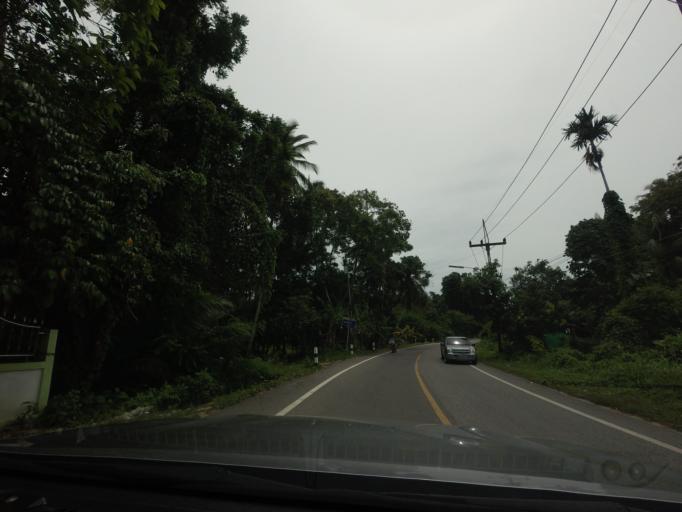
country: TH
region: Pattani
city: Kapho
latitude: 6.6431
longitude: 101.5503
